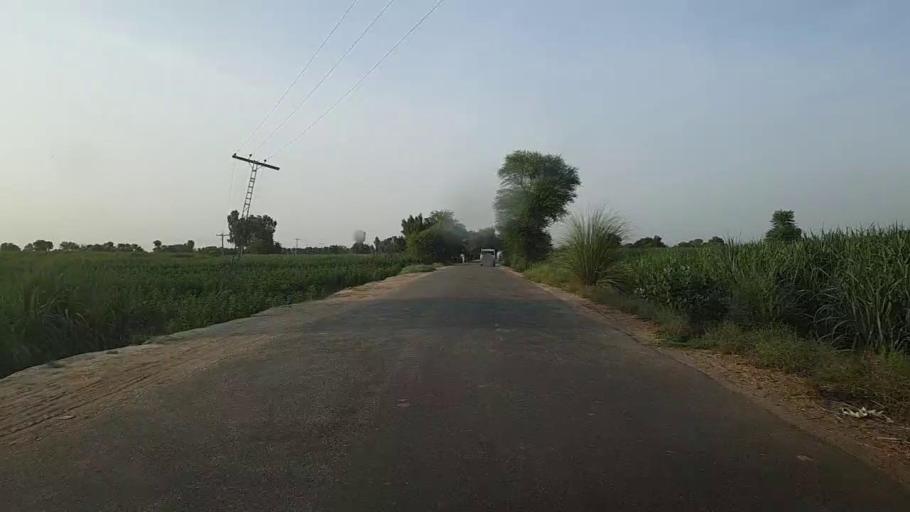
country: PK
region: Sindh
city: Ubauro
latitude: 28.1749
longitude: 69.8291
